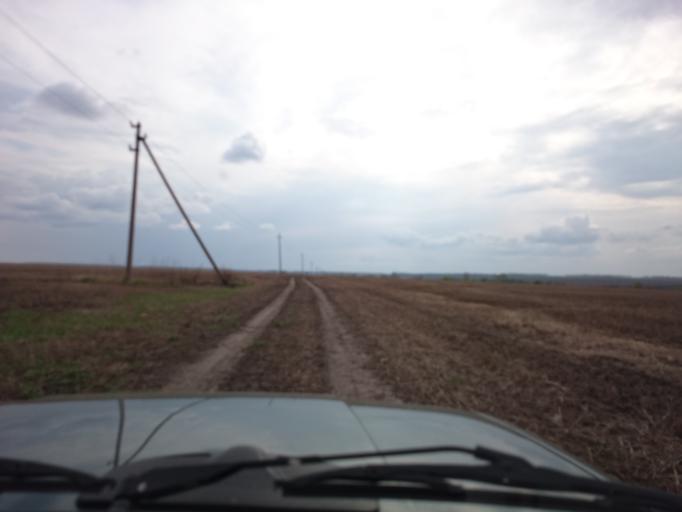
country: RU
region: Mordoviya
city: Kadoshkino
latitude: 54.0230
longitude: 44.4734
